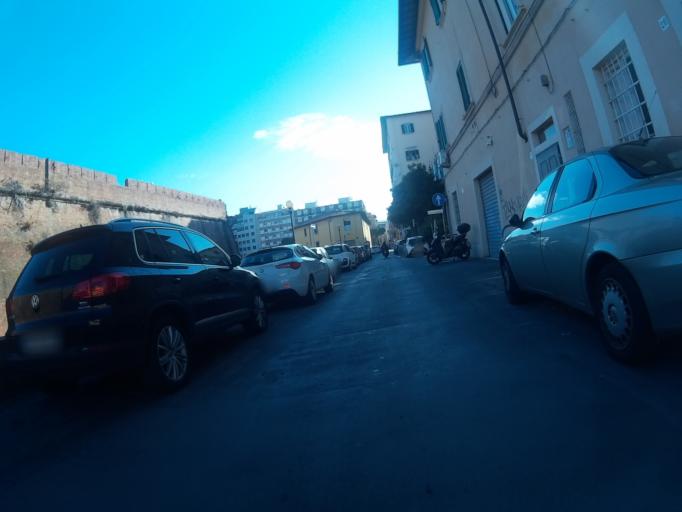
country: IT
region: Tuscany
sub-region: Provincia di Livorno
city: Livorno
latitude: 43.5548
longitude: 10.3100
